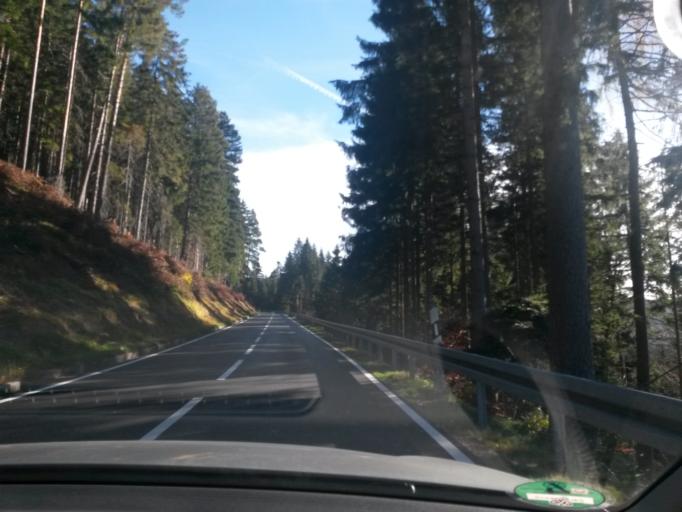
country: DE
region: Baden-Wuerttemberg
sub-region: Karlsruhe Region
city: Bad Rippoldsau-Schapbach
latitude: 48.4527
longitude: 8.2900
